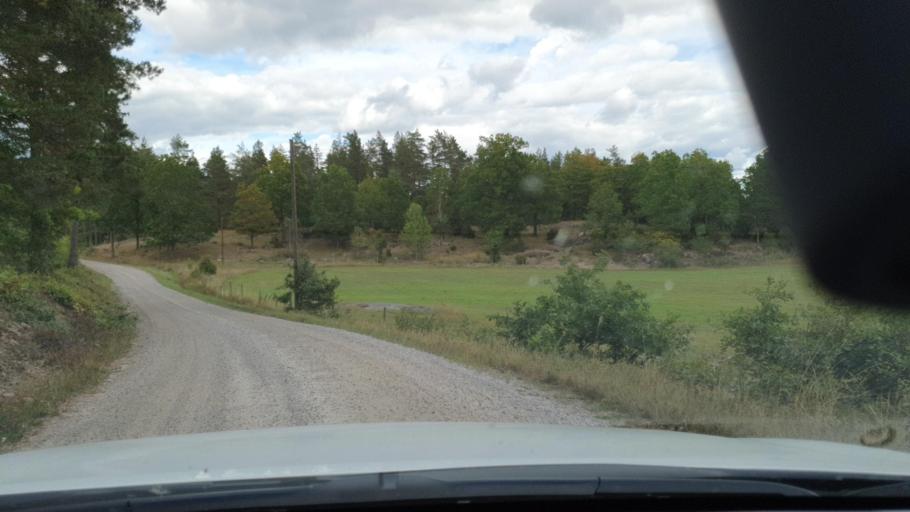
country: SE
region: Kalmar
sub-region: Vasterviks Kommun
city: Vaestervik
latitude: 57.7238
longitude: 16.4785
